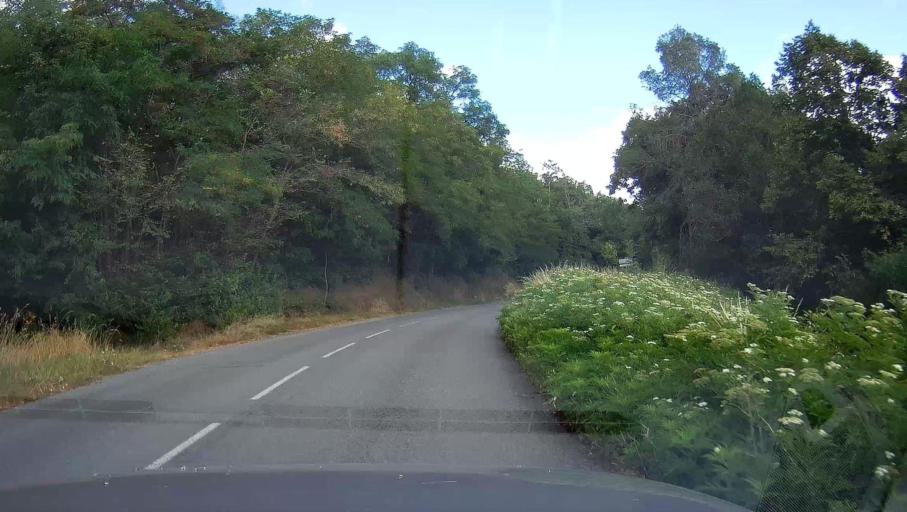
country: FR
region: Rhone-Alpes
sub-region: Departement du Rhone
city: Cogny
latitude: 45.9781
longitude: 4.5967
